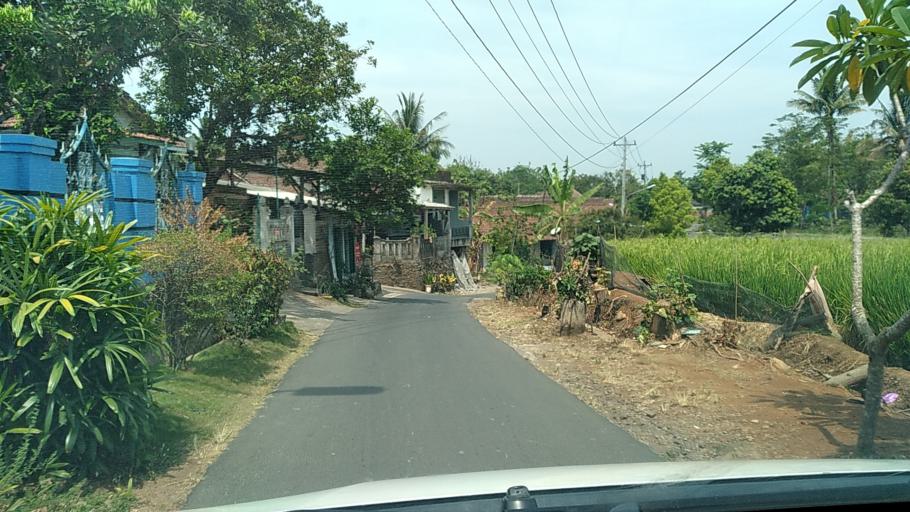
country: ID
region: Central Java
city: Ungaran
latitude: -7.0790
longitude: 110.3108
